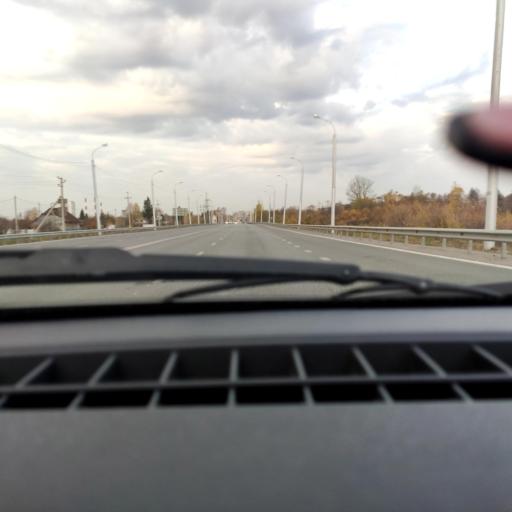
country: RU
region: Bashkortostan
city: Ufa
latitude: 54.8087
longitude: 56.1626
